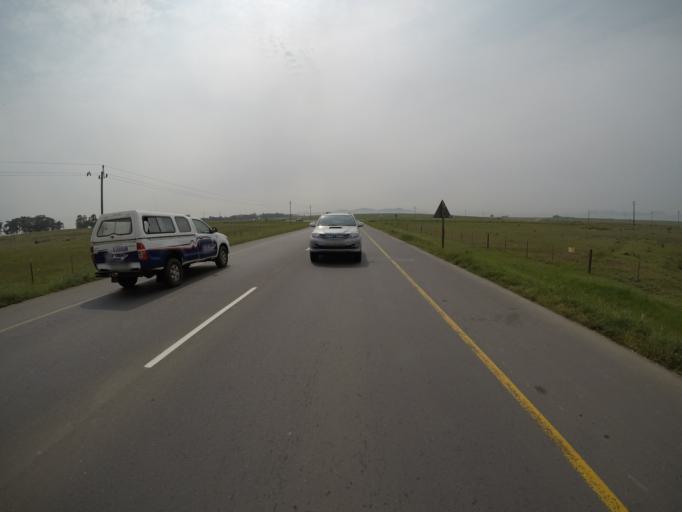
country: ZA
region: Western Cape
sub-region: City of Cape Town
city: Kraaifontein
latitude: -33.6988
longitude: 18.7059
